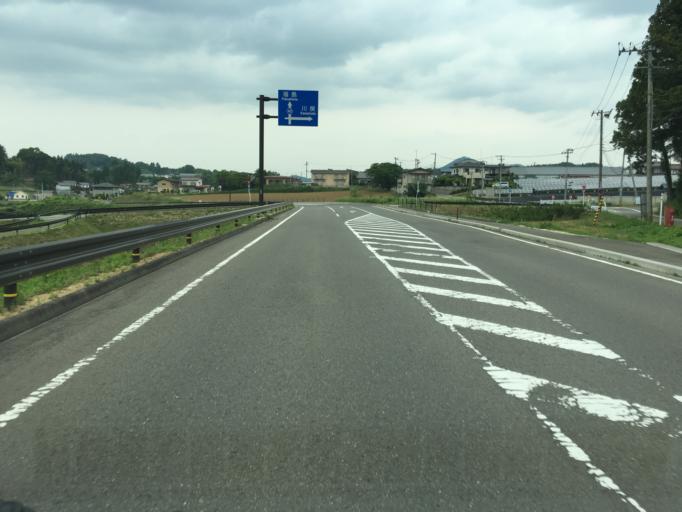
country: JP
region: Fukushima
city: Fukushima-shi
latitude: 37.6497
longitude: 140.5345
